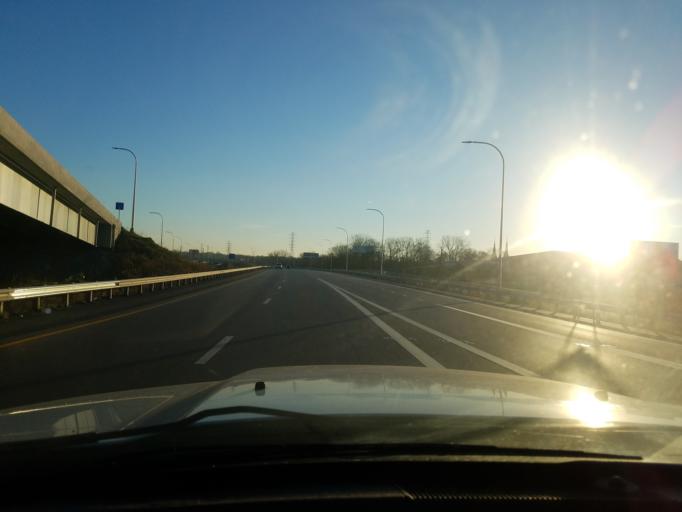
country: US
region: Indiana
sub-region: Clark County
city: Jeffersonville
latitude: 38.2604
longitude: -85.7345
